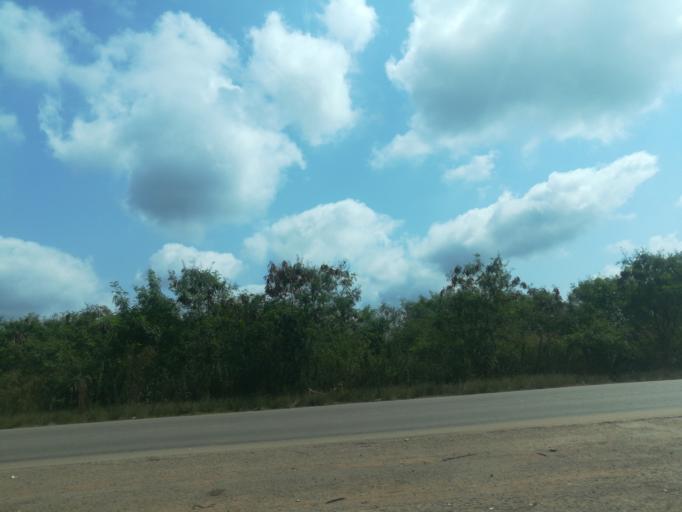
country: NG
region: Oyo
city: Moniya
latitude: 7.5871
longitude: 3.9143
